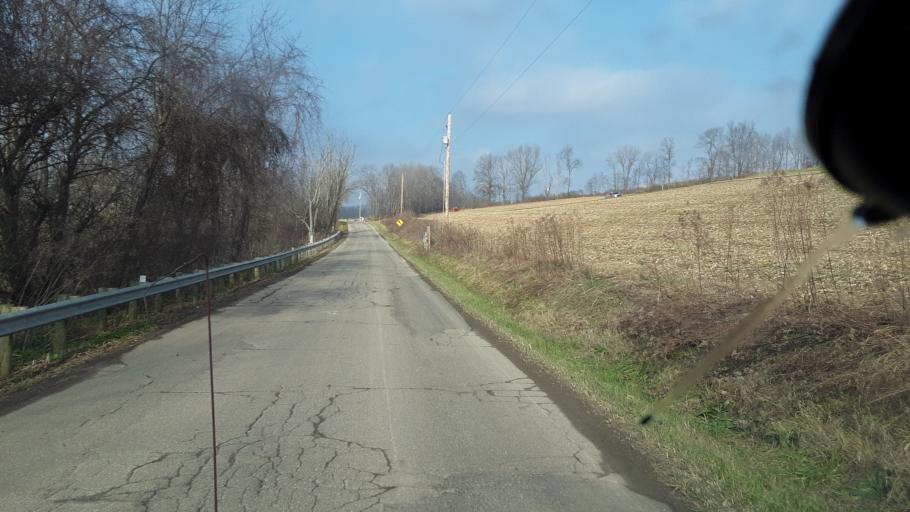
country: US
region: Ohio
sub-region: Knox County
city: Oak Hill
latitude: 40.4406
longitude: -82.2129
